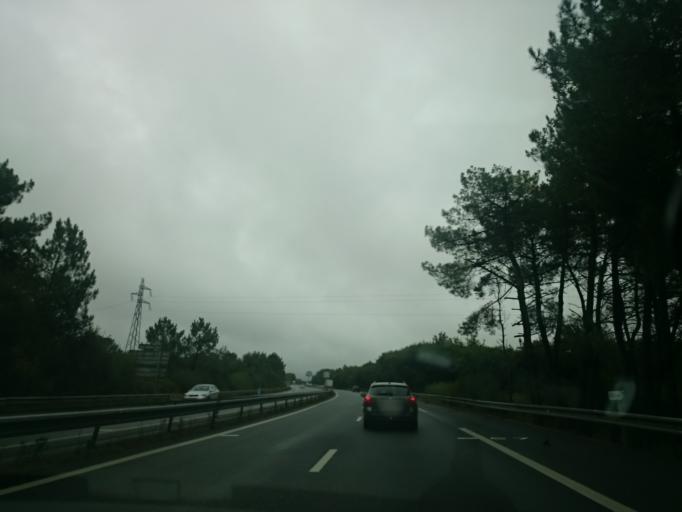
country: FR
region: Brittany
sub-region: Departement du Morbihan
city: Auray
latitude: 47.6867
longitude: -3.0305
